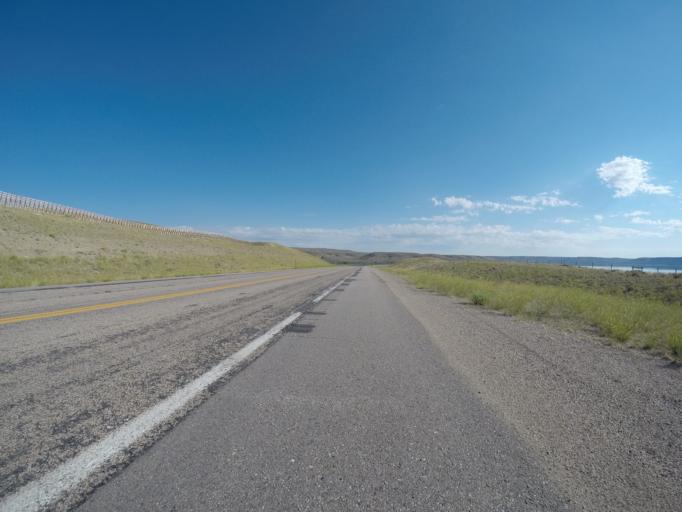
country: US
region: Wyoming
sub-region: Lincoln County
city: Kemmerer
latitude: 42.0775
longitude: -110.1604
